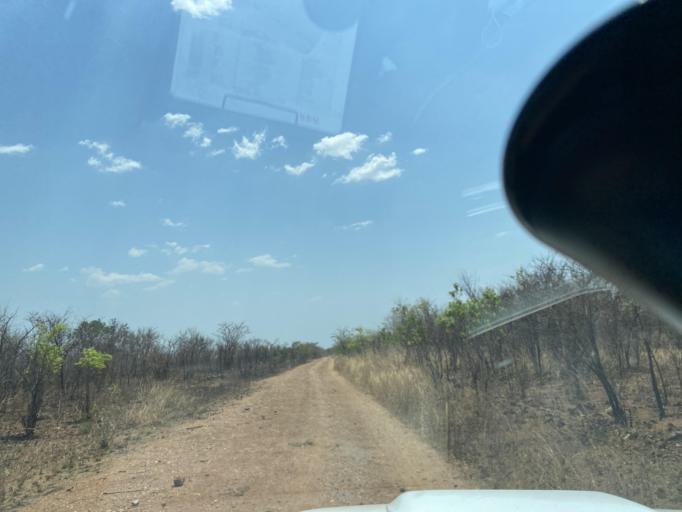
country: ZM
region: Lusaka
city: Lusaka
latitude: -15.5065
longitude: 27.9774
